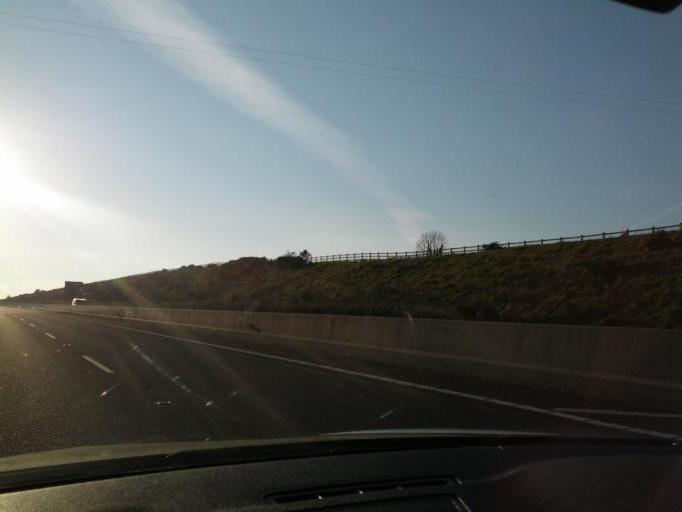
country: IE
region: Munster
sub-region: North Tipperary
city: Roscrea
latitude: 52.9150
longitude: -7.8224
